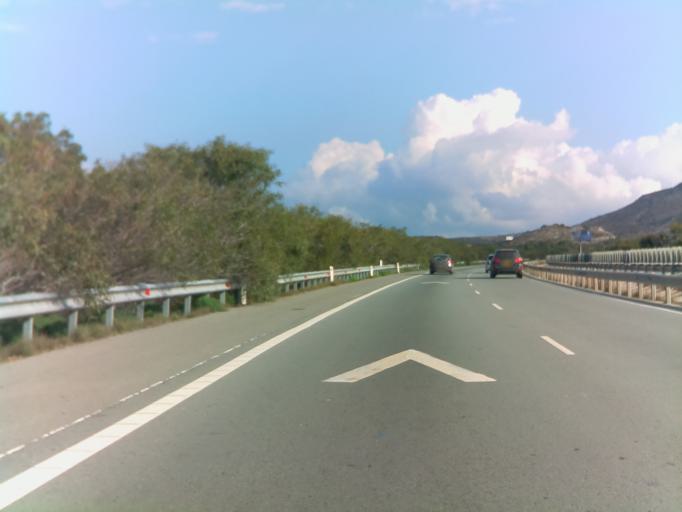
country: CY
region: Larnaka
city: Kofinou
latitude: 34.7732
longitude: 33.3372
